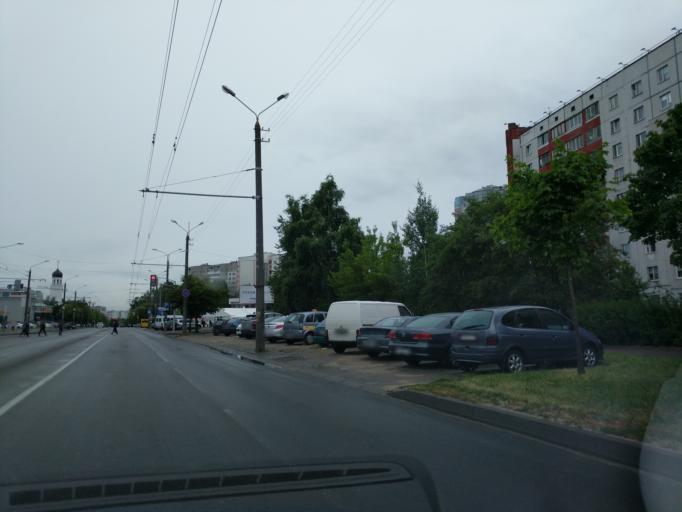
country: BY
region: Minsk
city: Novoye Medvezhino
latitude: 53.8625
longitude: 27.4793
